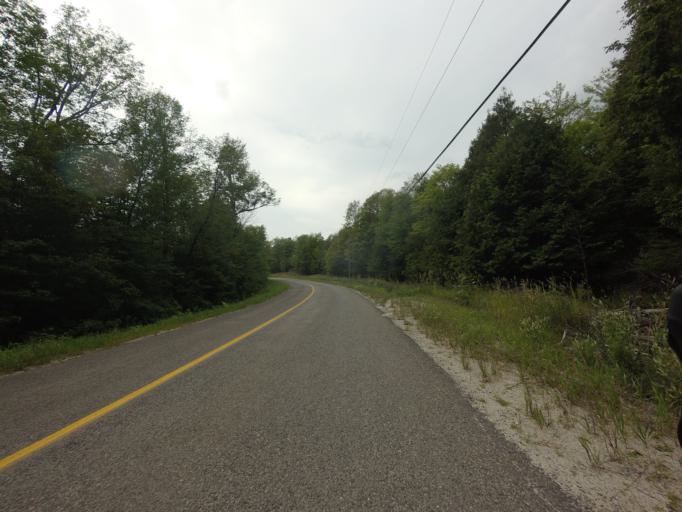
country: CA
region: Ontario
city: Perth
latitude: 44.8406
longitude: -76.5667
